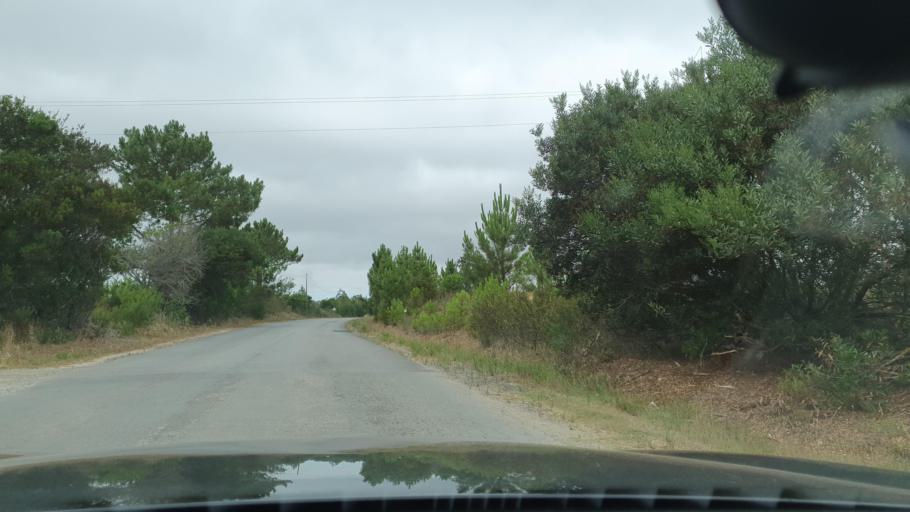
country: PT
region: Beja
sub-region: Odemira
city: Sao Teotonio
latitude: 37.5015
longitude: -8.6877
